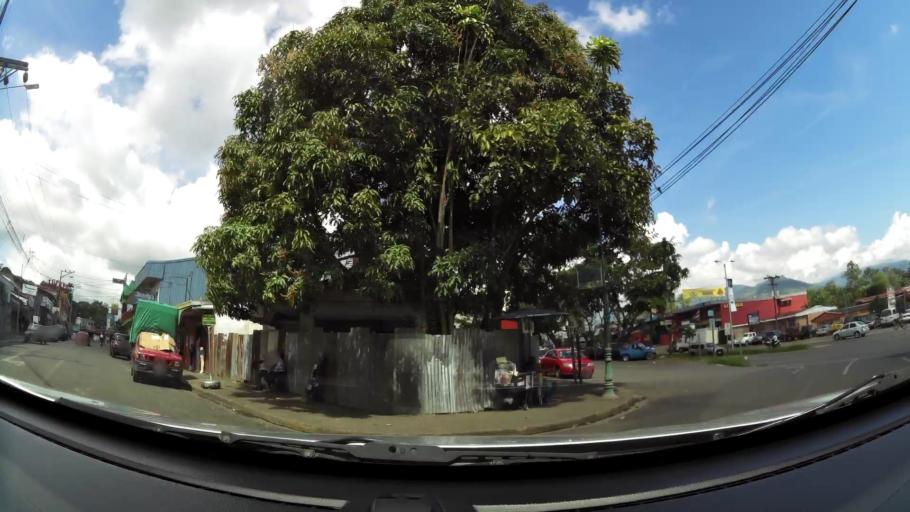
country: CR
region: San Jose
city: San Isidro
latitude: 9.3764
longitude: -83.7035
